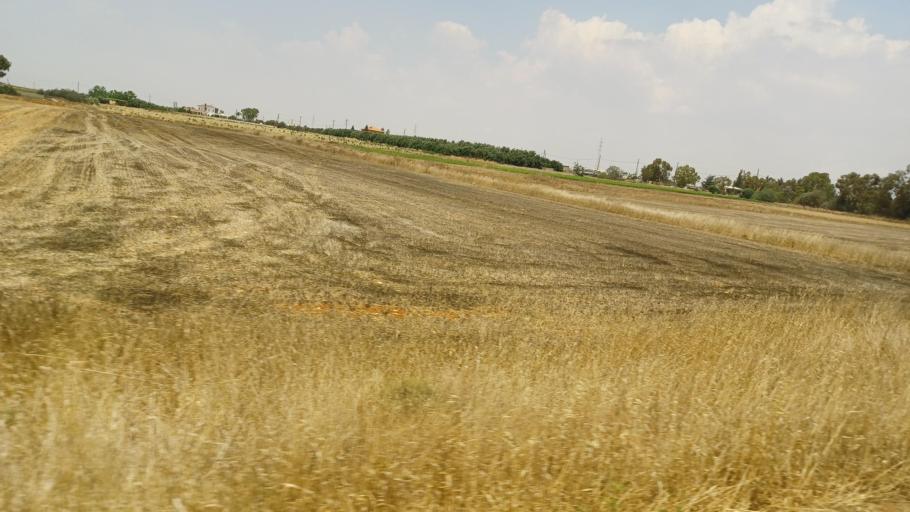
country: CY
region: Ammochostos
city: Liopetri
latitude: 34.9922
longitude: 33.8518
